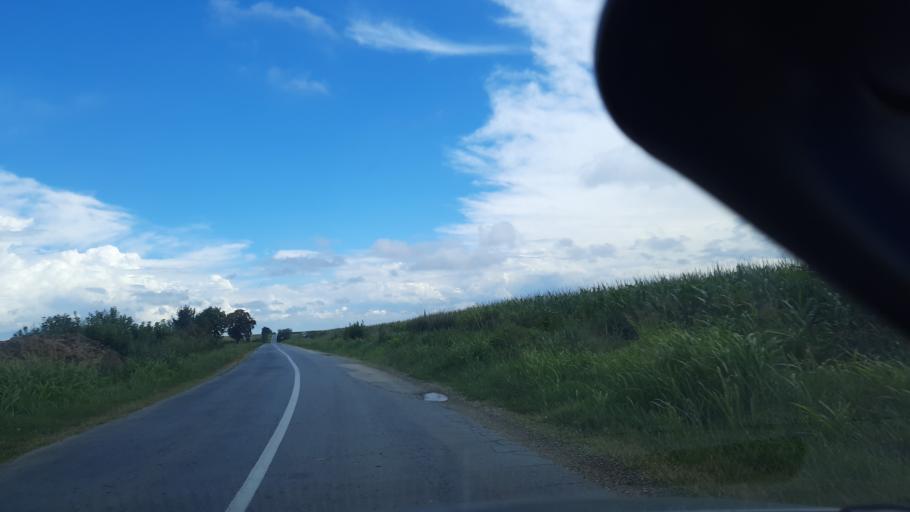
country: RS
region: Autonomna Pokrajina Vojvodina
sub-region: Sremski Okrug
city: Sremska Mitrovica
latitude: 45.0994
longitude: 19.5674
